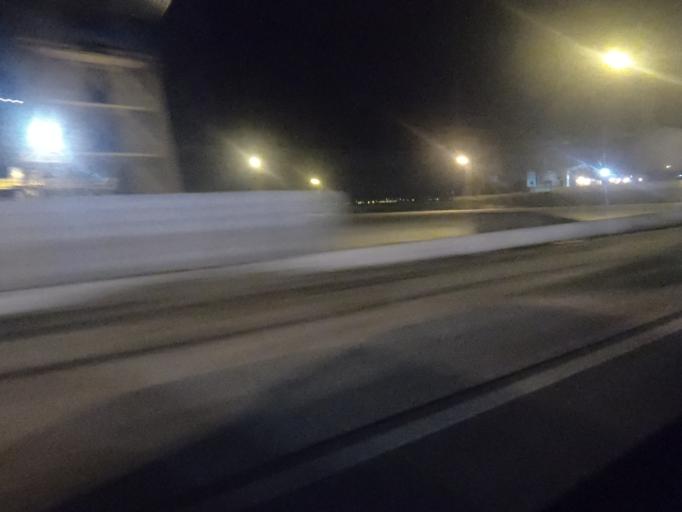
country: PT
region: Setubal
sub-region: Setubal
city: Setubal
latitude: 38.5089
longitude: -8.8509
